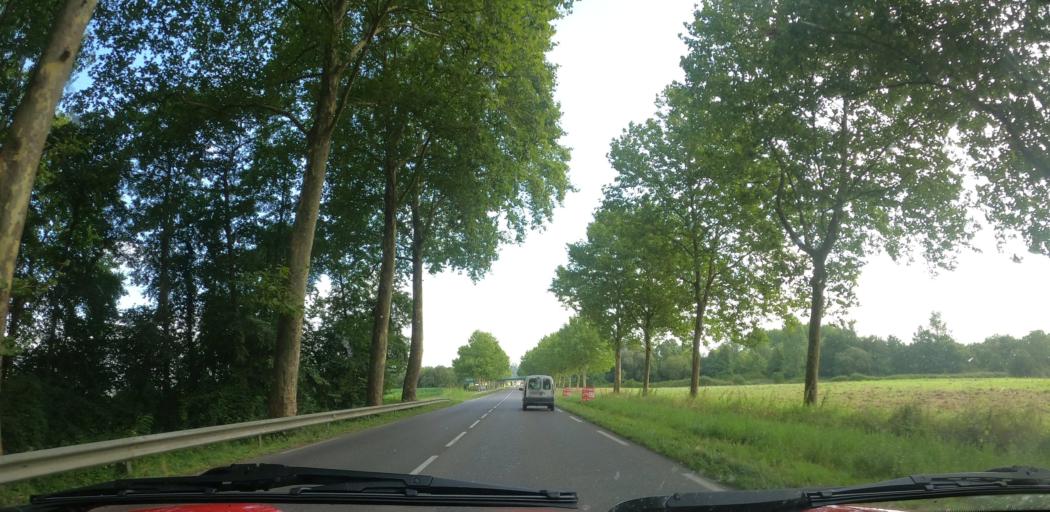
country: FR
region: Aquitaine
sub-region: Departement des Landes
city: Peyrehorade
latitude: 43.5329
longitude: -1.1100
